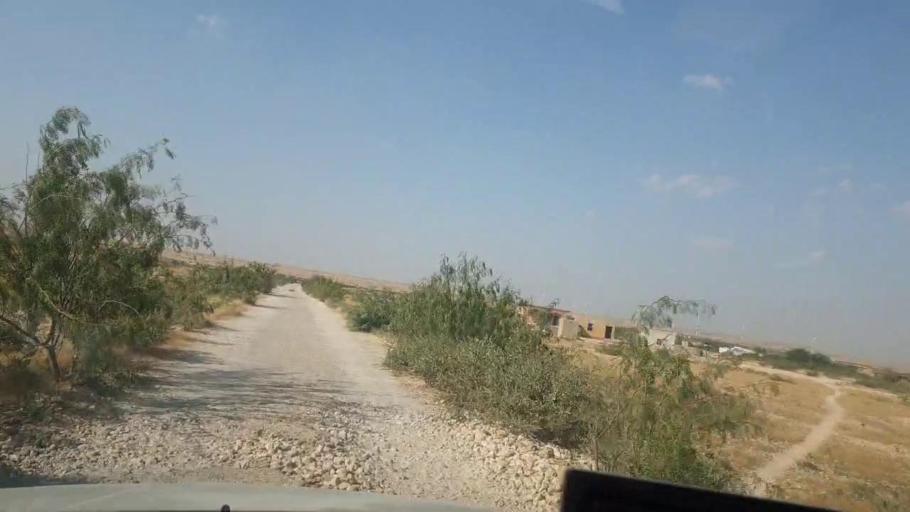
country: PK
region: Sindh
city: Daro Mehar
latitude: 25.0716
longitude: 68.0967
